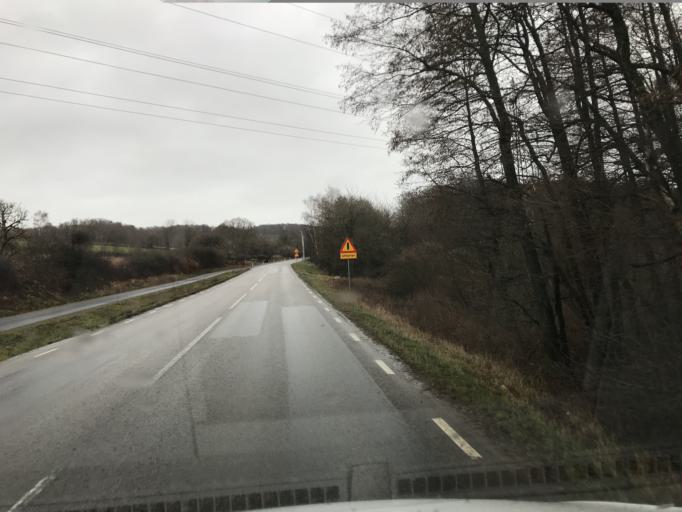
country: SE
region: Skane
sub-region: Bastads Kommun
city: Forslov
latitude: 56.3525
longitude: 12.8369
